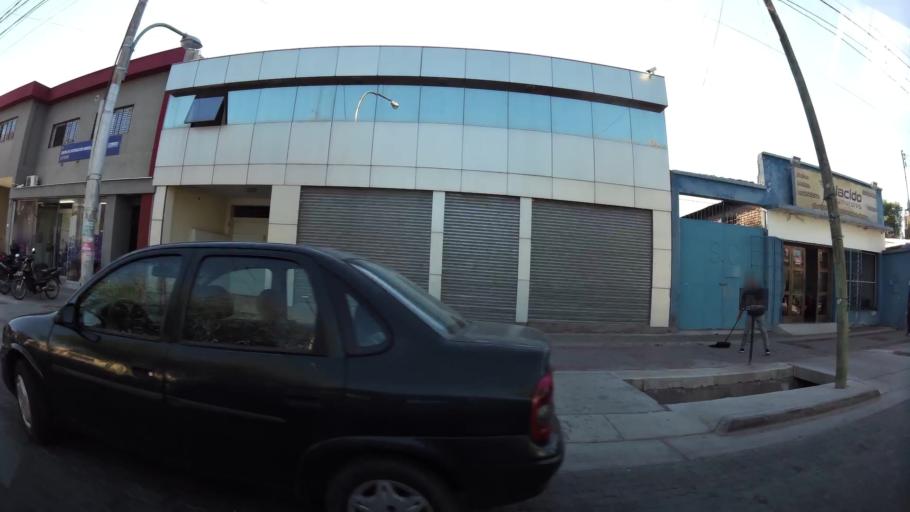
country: AR
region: Mendoza
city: Las Heras
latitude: -32.8589
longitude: -68.8331
